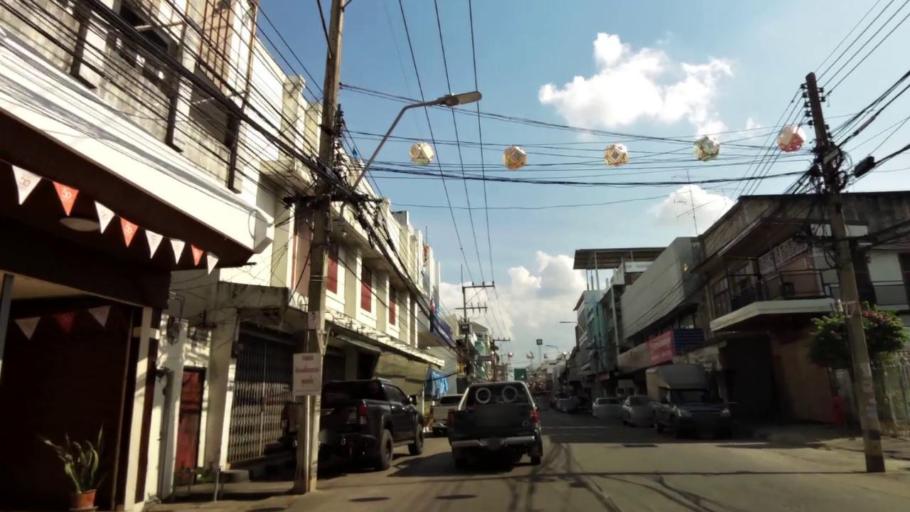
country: TH
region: Phrae
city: Phrae
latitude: 18.1391
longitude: 100.1465
